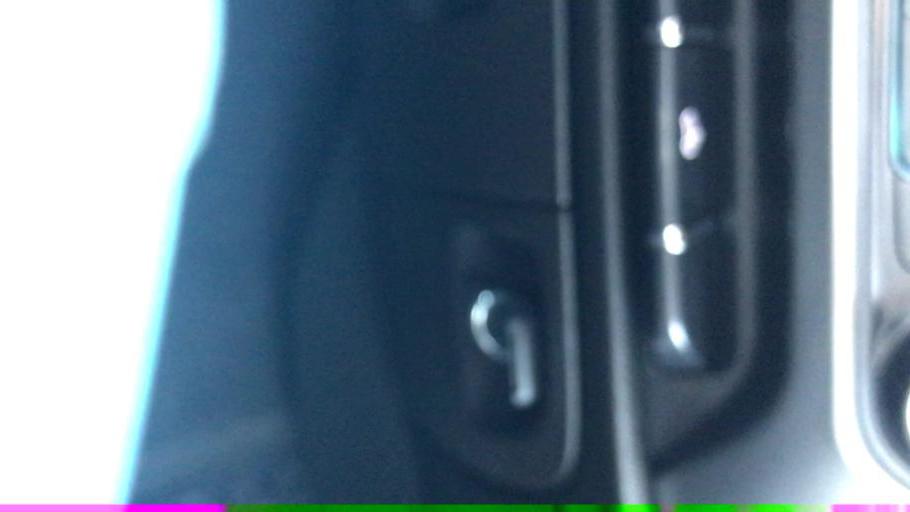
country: US
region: Texas
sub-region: Denton County
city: Double Oak
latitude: 33.0463
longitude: -97.1203
